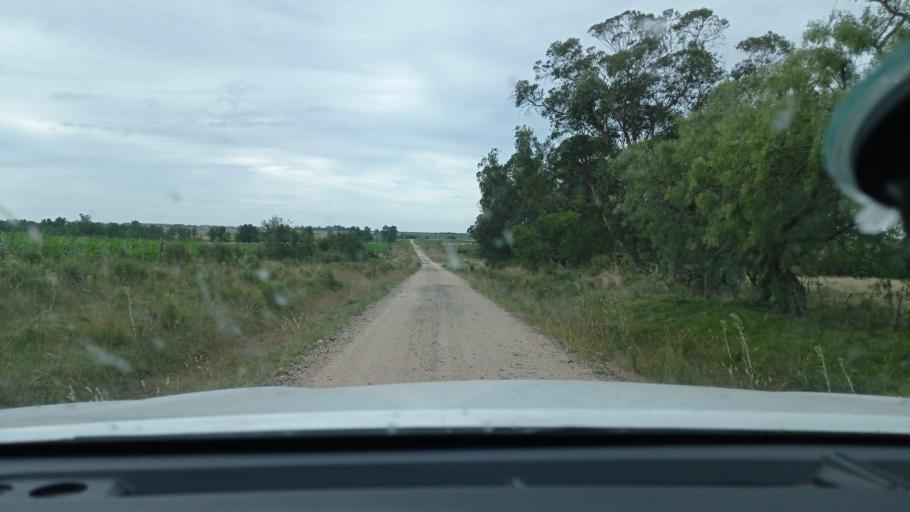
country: UY
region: Florida
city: Casupa
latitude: -34.1318
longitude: -55.7791
